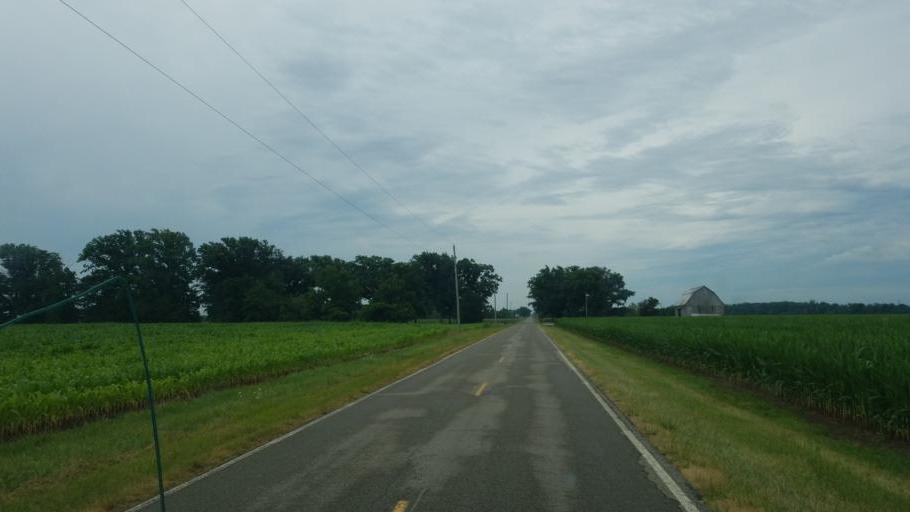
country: US
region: Ohio
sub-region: Defiance County
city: Hicksville
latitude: 41.2872
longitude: -84.6895
